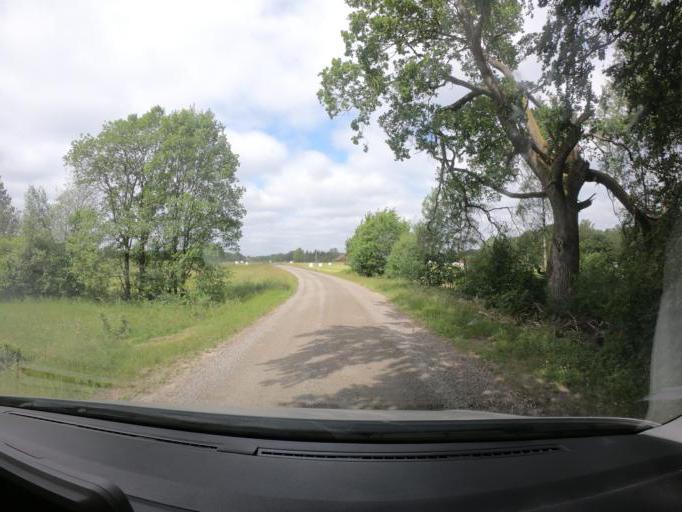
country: SE
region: Skane
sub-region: Hassleholms Kommun
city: Sosdala
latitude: 56.1039
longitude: 13.6619
